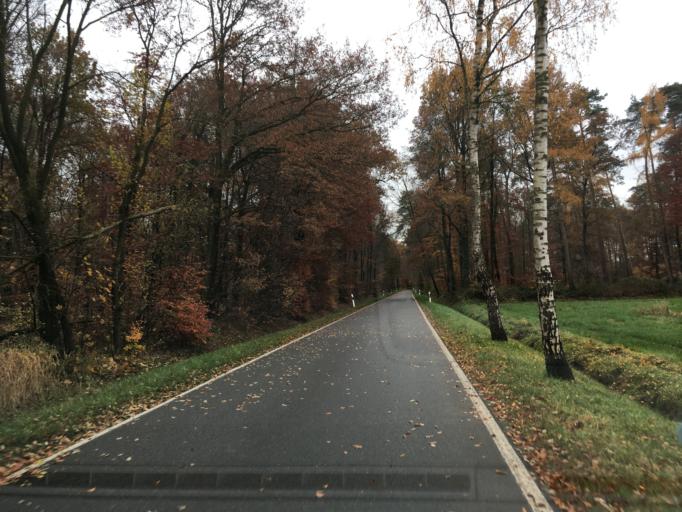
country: DE
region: North Rhine-Westphalia
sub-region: Regierungsbezirk Munster
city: Gescher
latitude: 52.0012
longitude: 6.9972
